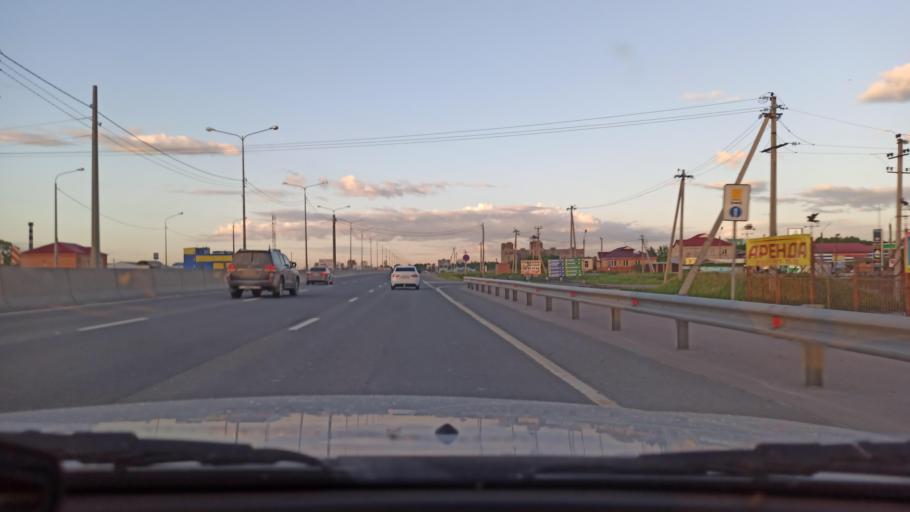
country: RU
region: Vologda
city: Vologda
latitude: 59.2142
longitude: 39.7898
